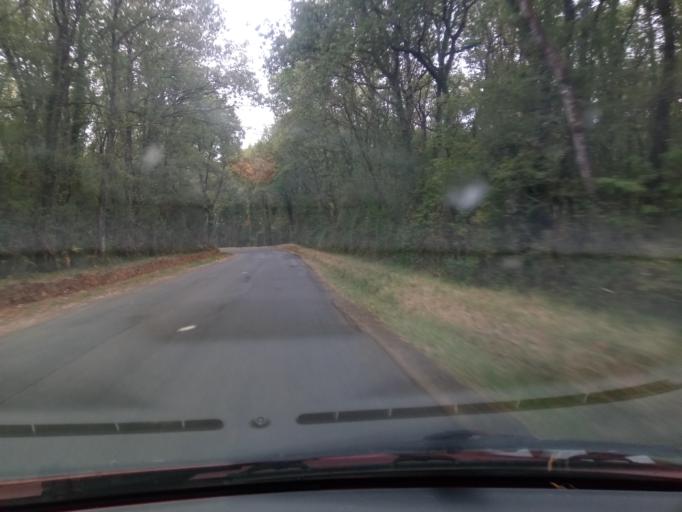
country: FR
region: Poitou-Charentes
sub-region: Departement de la Vienne
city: Saint-Savin
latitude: 46.5245
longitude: 0.7736
